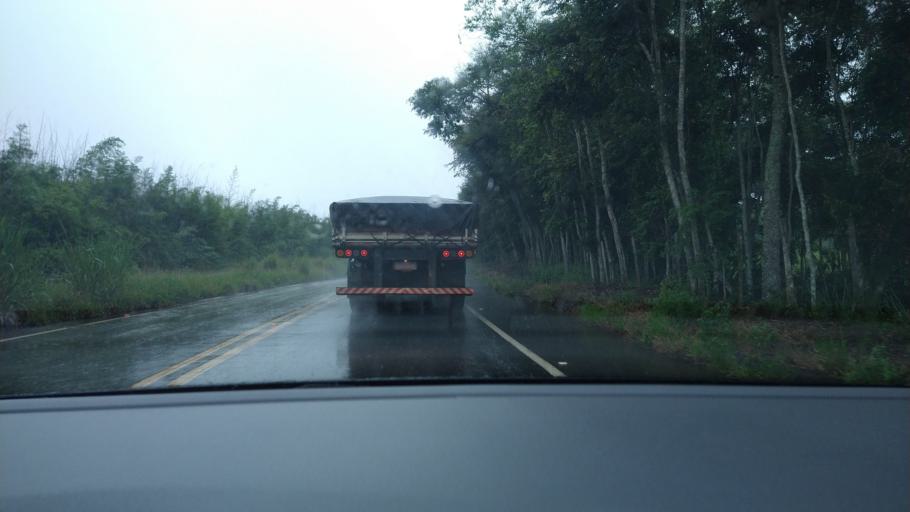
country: BR
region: Minas Gerais
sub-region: Ponte Nova
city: Ponte Nova
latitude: -20.5730
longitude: -42.8745
